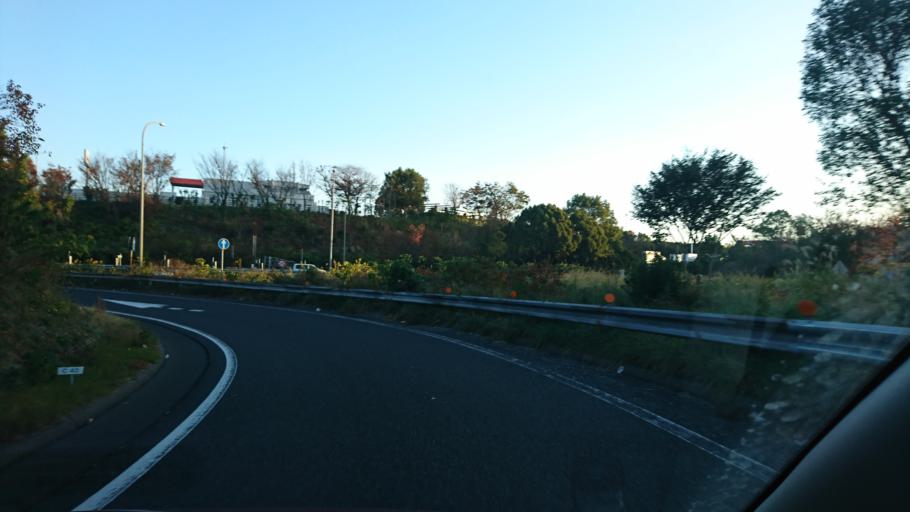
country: JP
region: Hyogo
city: Akashi
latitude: 34.7033
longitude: 134.9565
